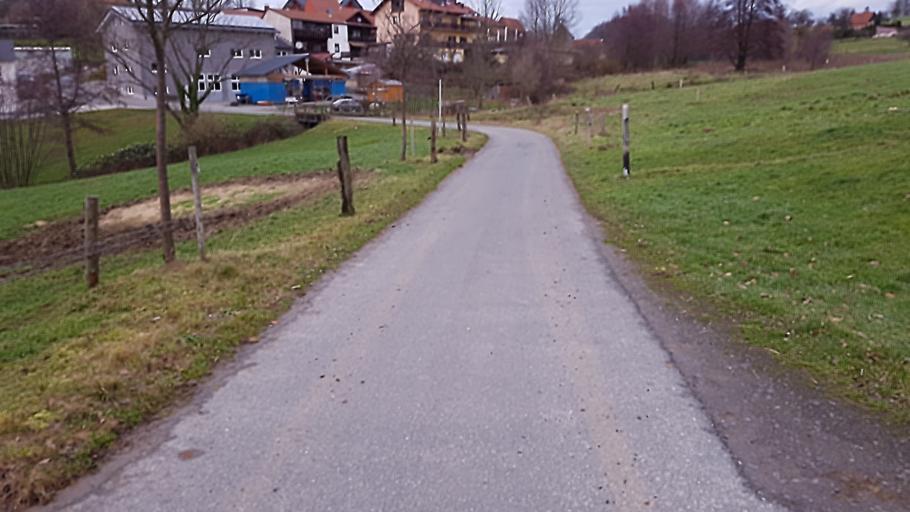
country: DE
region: Hesse
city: Reichelsheim
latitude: 49.7151
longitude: 8.8065
